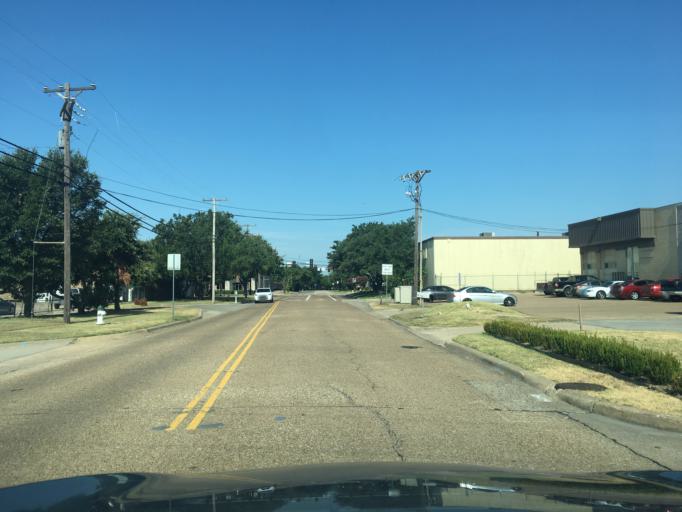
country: US
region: Texas
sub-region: Dallas County
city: Addison
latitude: 32.9581
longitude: -96.8369
